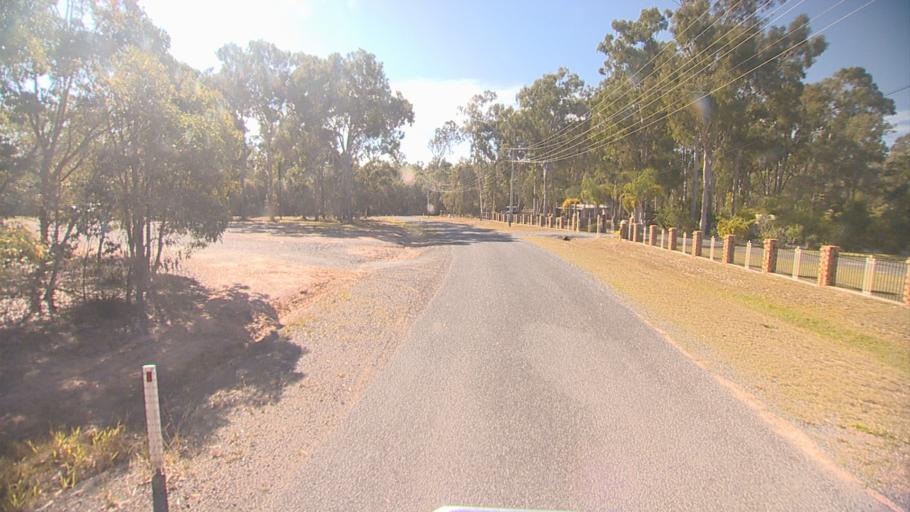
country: AU
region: Queensland
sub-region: Logan
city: Park Ridge South
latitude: -27.7235
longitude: 152.9735
